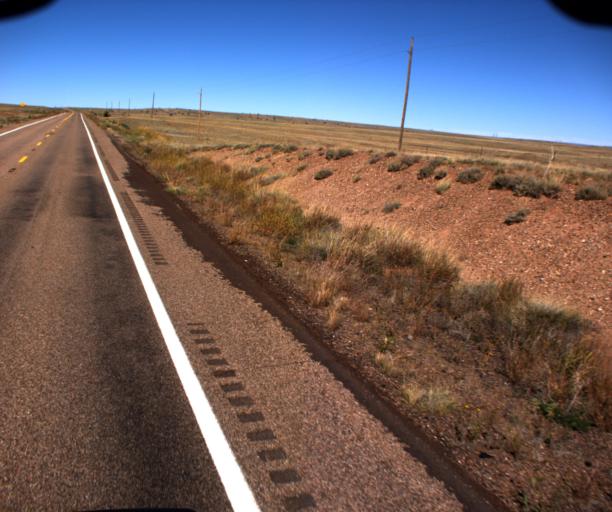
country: US
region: Arizona
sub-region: Apache County
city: Saint Johns
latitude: 34.5166
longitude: -109.4507
